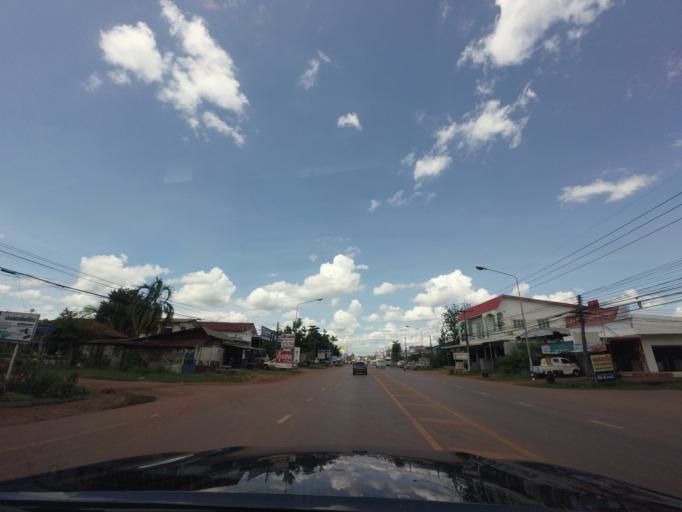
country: TH
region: Changwat Udon Thani
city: Ban Dung
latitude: 17.6839
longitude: 103.2556
